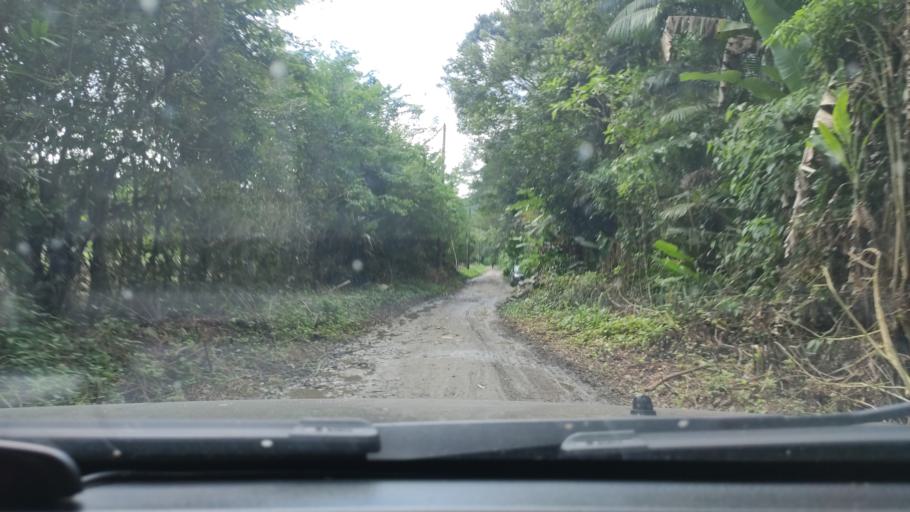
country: BR
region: Sao Paulo
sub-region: Sao Sebastiao
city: Sao Sebastiao
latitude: -23.7329
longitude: -45.4936
